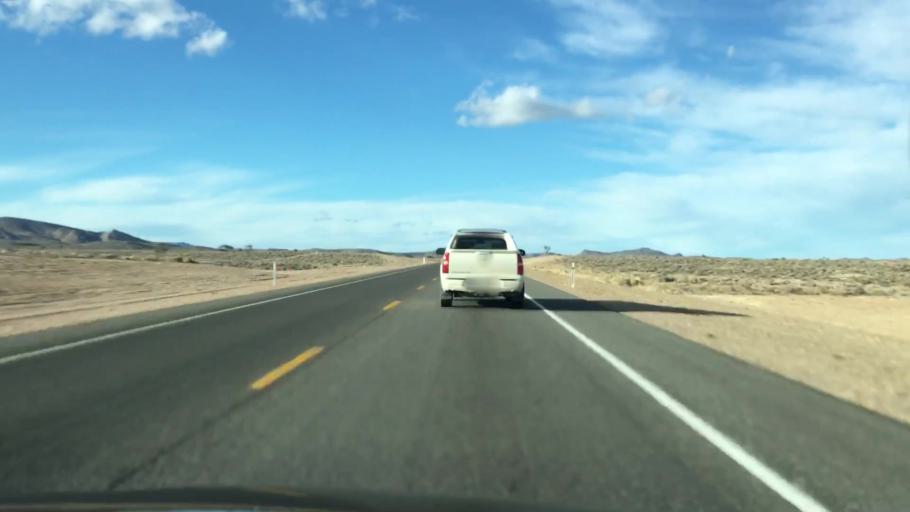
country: US
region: Nevada
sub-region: Esmeralda County
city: Goldfield
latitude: 37.5780
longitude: -117.2040
